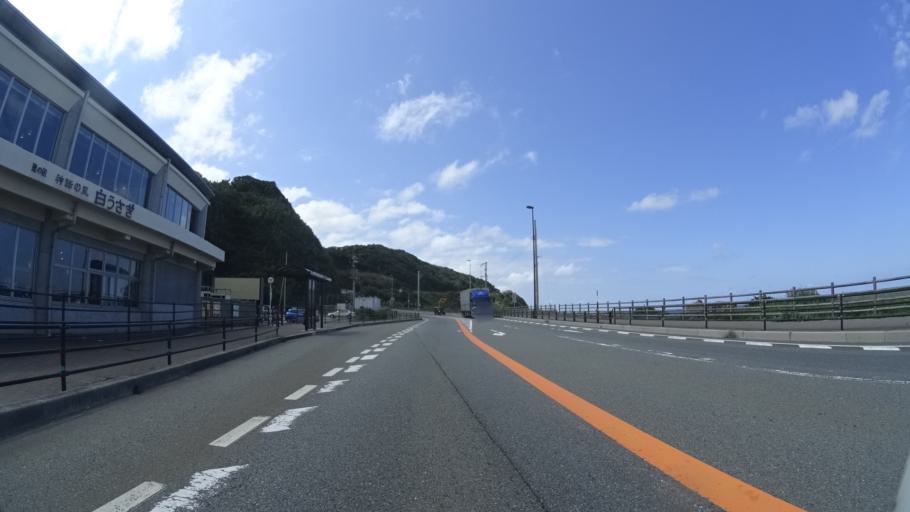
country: JP
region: Tottori
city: Tottori
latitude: 35.5257
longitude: 134.1146
